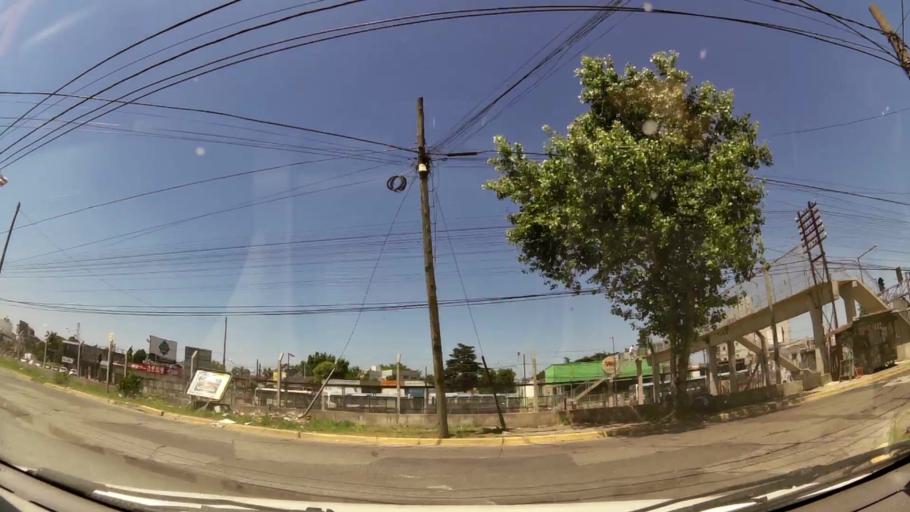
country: AR
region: Buenos Aires
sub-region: Partido de Merlo
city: Merlo
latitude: -34.6650
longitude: -58.6969
